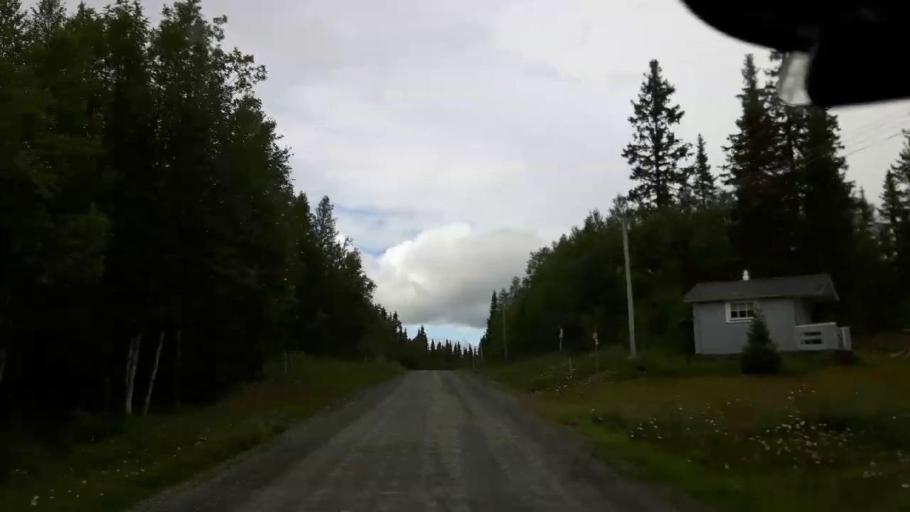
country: SE
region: Jaemtland
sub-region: Krokoms Kommun
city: Valla
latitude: 63.7272
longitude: 13.8416
